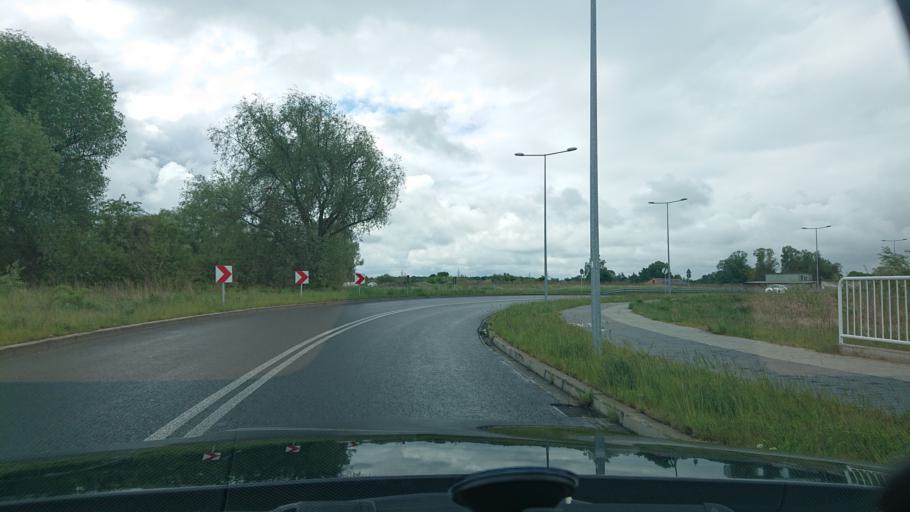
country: PL
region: Greater Poland Voivodeship
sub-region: Powiat gnieznienski
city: Gniezno
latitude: 52.5244
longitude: 17.6237
